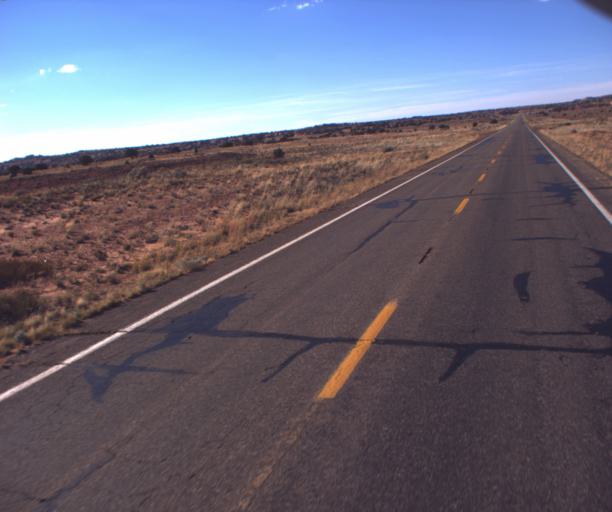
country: US
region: Arizona
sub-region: Coconino County
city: Kaibito
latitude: 36.6086
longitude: -111.1819
